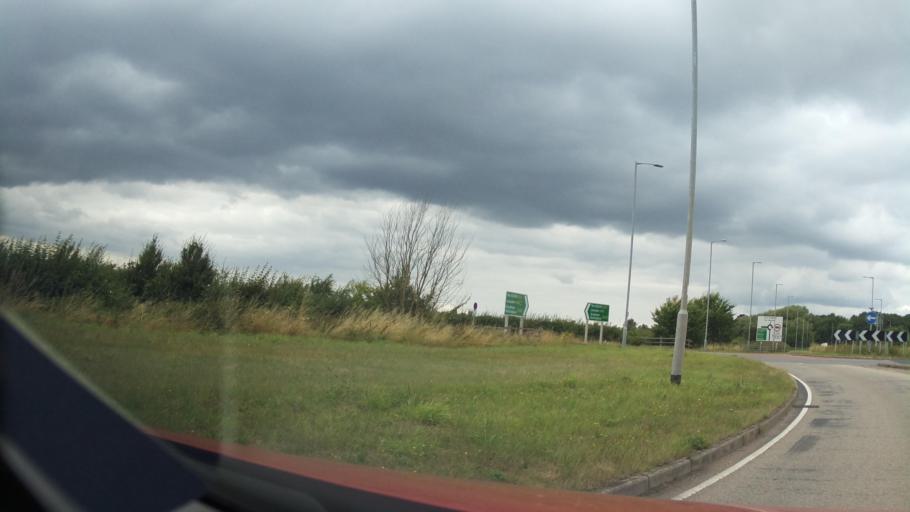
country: GB
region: England
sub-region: Nottinghamshire
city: Bingham
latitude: 52.9642
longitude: -0.9617
